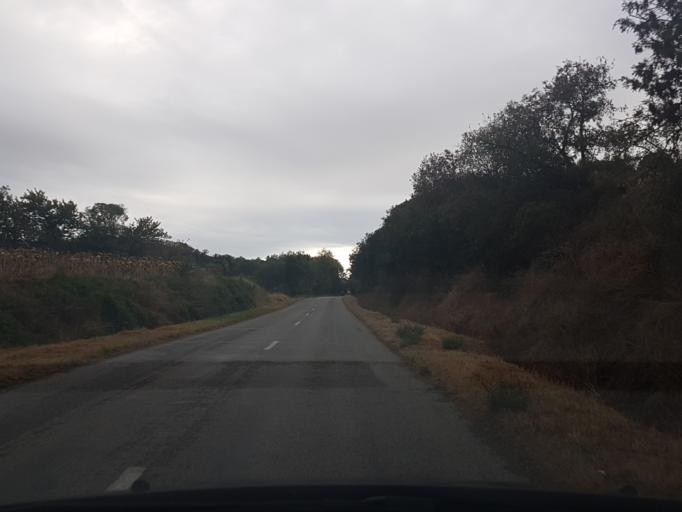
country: FR
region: Languedoc-Roussillon
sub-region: Departement de l'Aude
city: Bram
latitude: 43.1868
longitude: 2.0403
